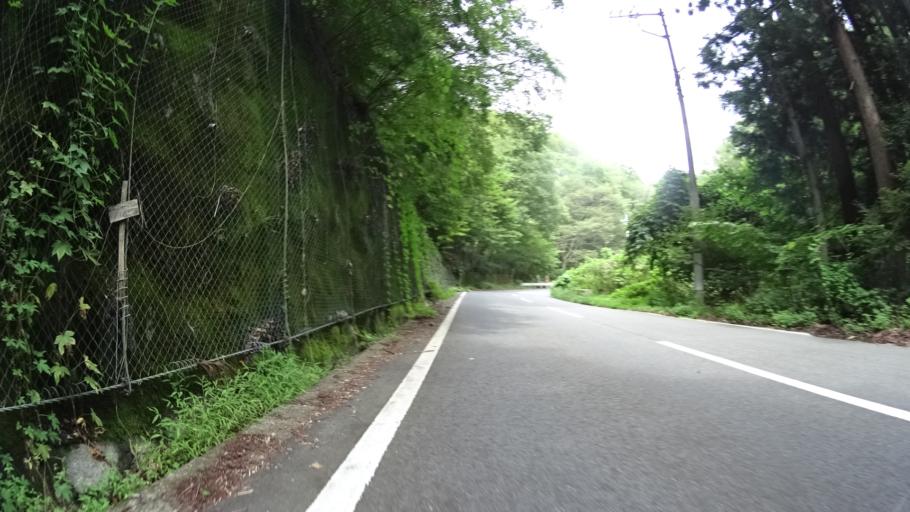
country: JP
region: Yamanashi
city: Kofu-shi
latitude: 35.7610
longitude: 138.5432
